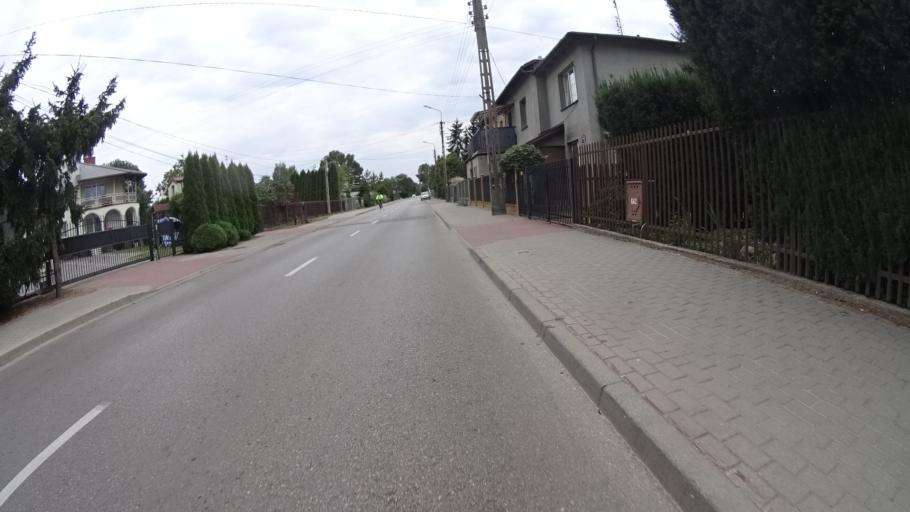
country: PL
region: Masovian Voivodeship
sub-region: Powiat pruszkowski
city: Granica
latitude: 52.1387
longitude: 20.7968
